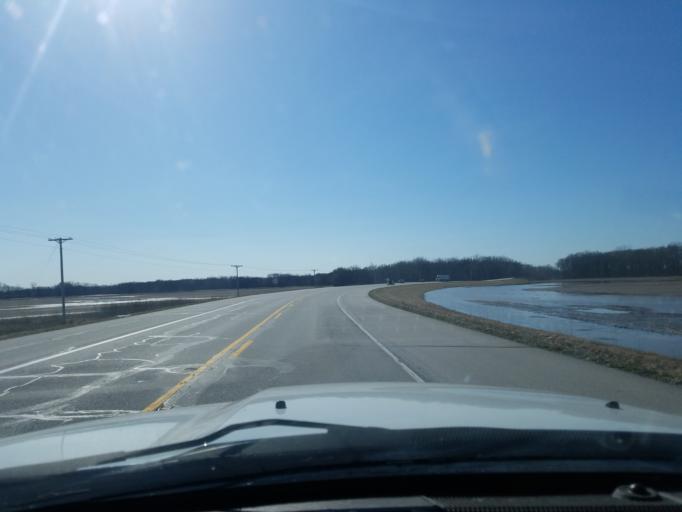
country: US
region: Indiana
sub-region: Shelby County
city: Shelbyville
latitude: 39.4973
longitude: -85.8576
